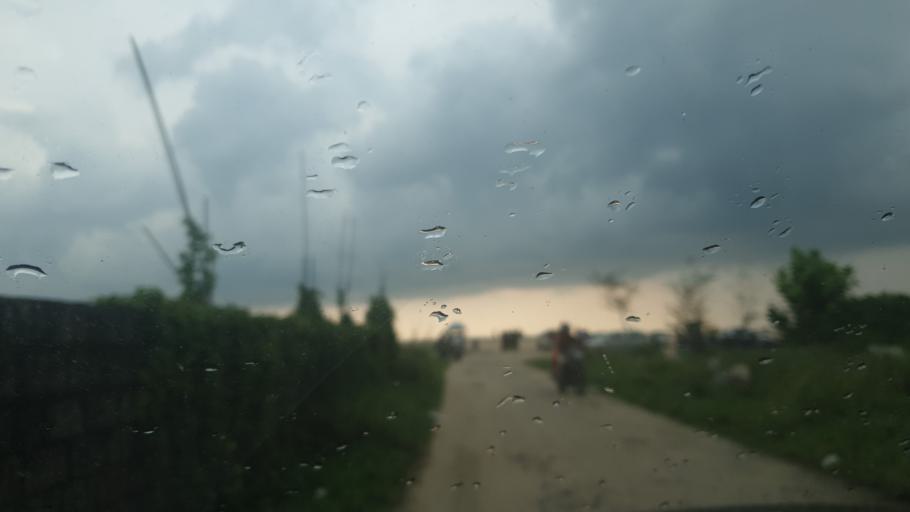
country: IN
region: Kerala
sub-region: Ernakulam
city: Cochin
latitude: 10.0059
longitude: 76.2174
